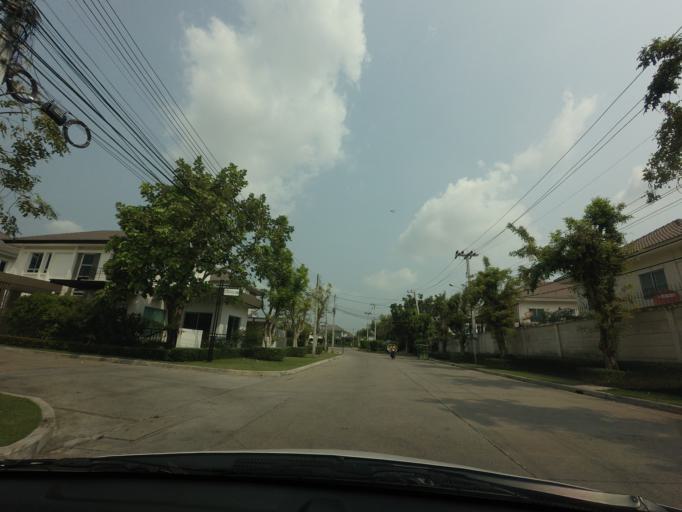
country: TH
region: Pathum Thani
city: Khlong Luang
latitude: 14.0018
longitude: 100.6602
